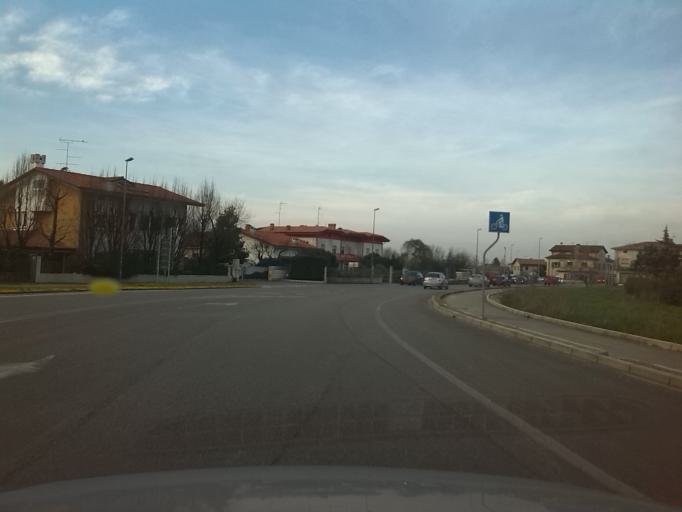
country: IT
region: Friuli Venezia Giulia
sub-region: Provincia di Udine
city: Corno di Rosazzo
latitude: 45.9893
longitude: 13.4466
